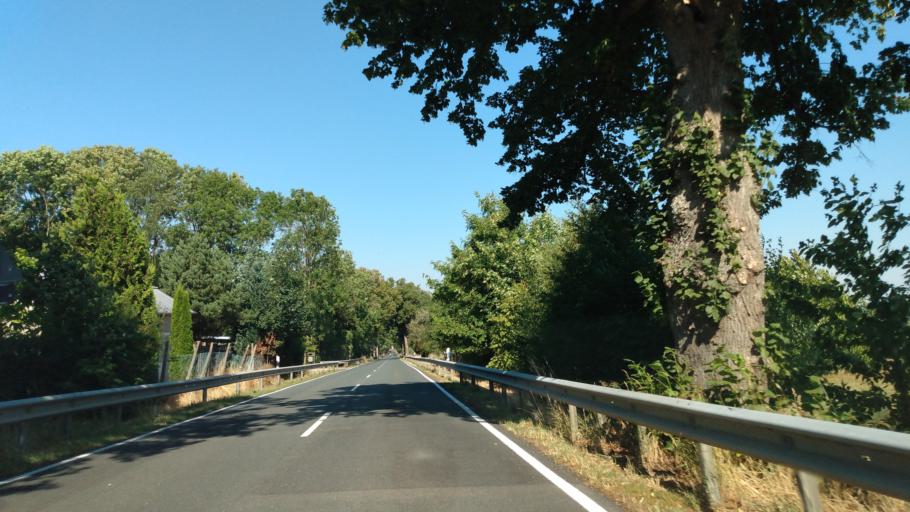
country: DE
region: Rheinland-Pfalz
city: Irmenach
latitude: 49.9174
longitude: 7.1988
